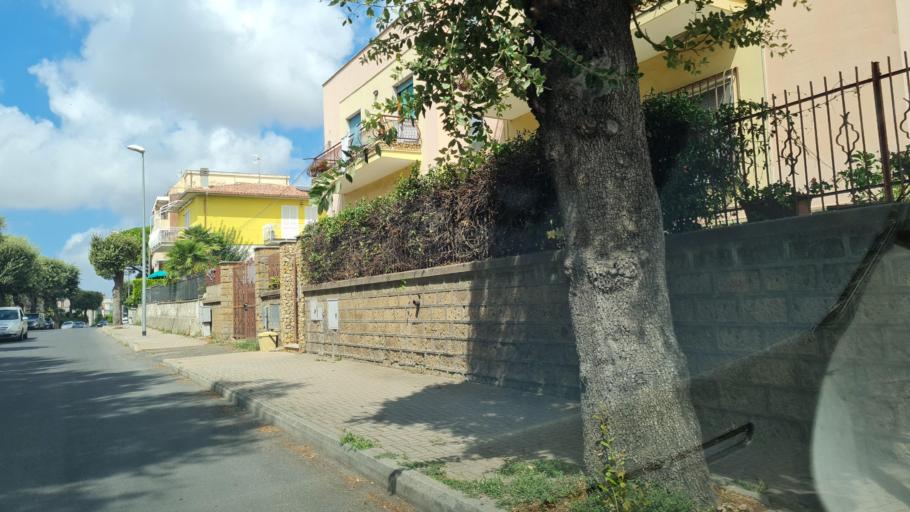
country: IT
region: Latium
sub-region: Provincia di Viterbo
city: Tarquinia
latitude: 42.2499
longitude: 11.7674
